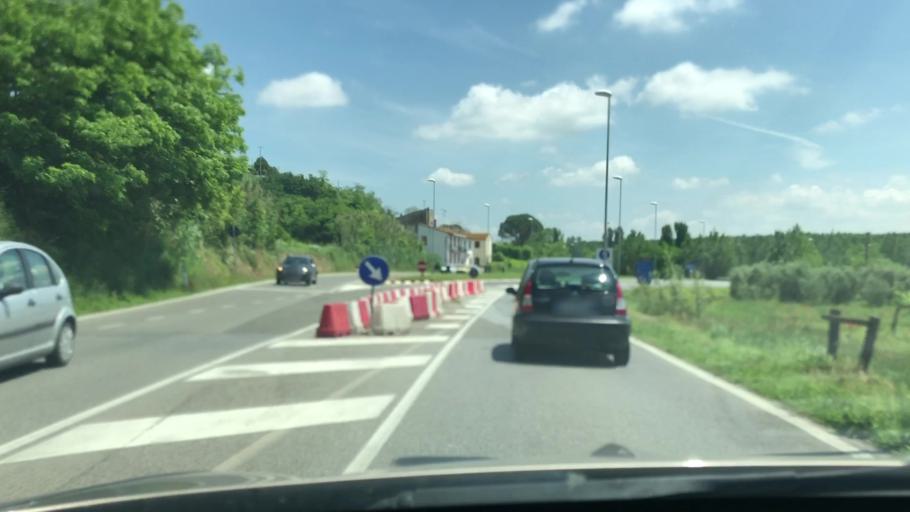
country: IT
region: Tuscany
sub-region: Province of Pisa
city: Forcoli
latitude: 43.6105
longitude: 10.6889
